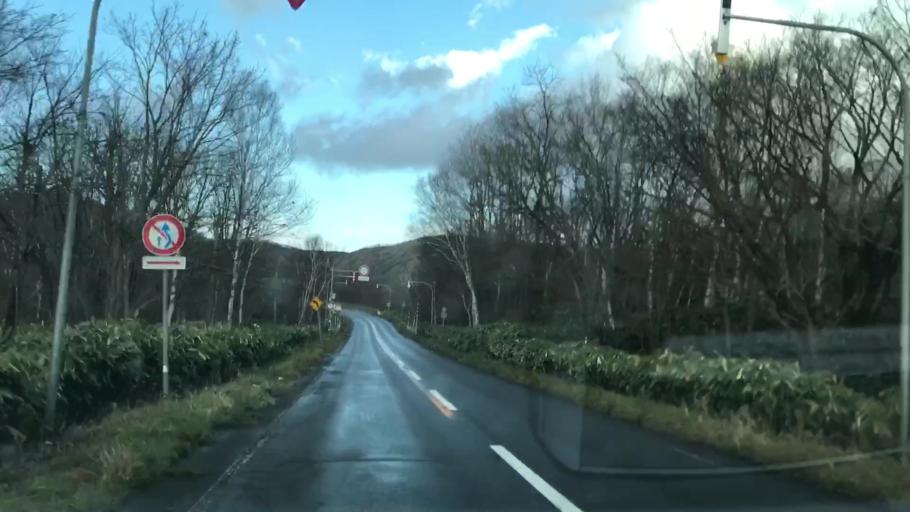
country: JP
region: Hokkaido
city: Yoichi
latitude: 43.3239
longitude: 140.5136
